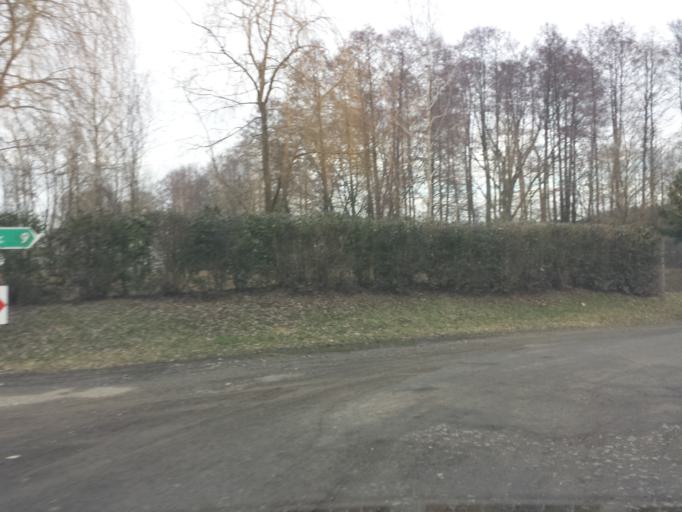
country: PL
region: Lodz Voivodeship
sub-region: Powiat wielunski
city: Osjakow
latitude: 51.2848
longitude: 18.7765
